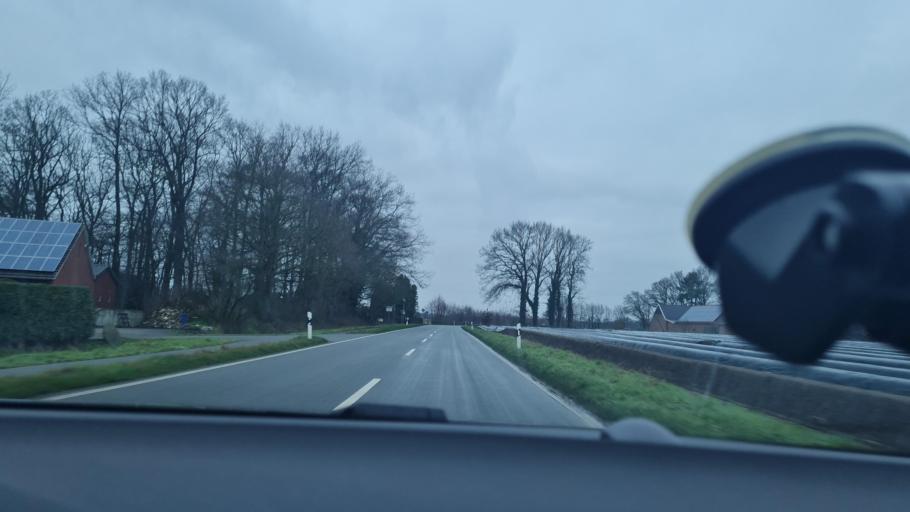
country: DE
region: North Rhine-Westphalia
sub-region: Regierungsbezirk Munster
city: Heiden
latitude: 51.7823
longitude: 6.9151
